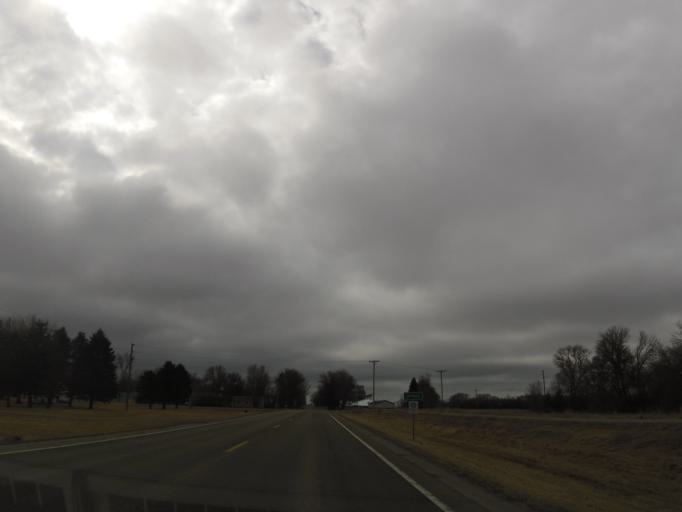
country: US
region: North Dakota
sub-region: Cass County
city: Casselton
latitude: 47.1094
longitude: -97.2181
